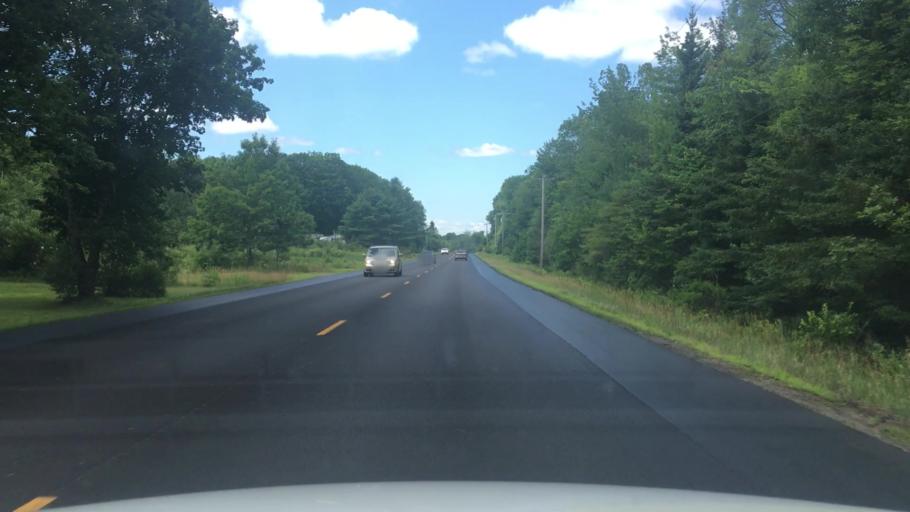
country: US
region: Maine
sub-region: Waldo County
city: Searsmont
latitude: 44.3988
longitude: -69.1505
